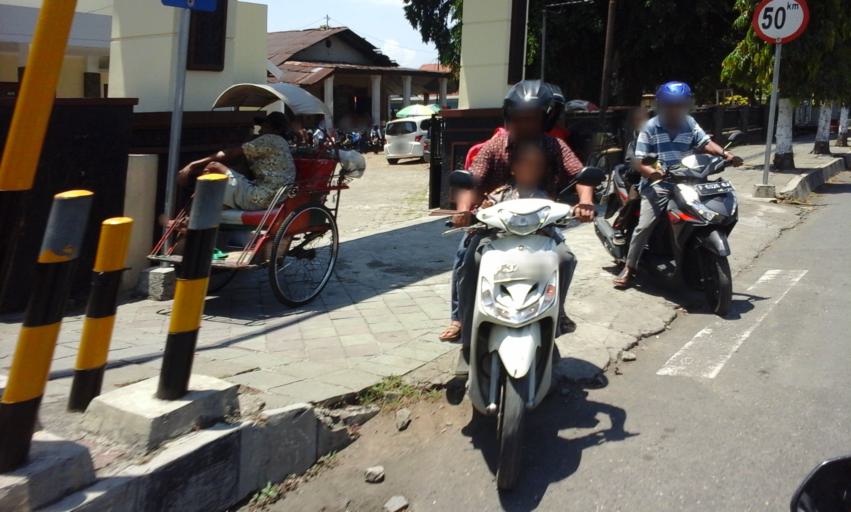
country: ID
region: East Java
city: Krajan
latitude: -8.1617
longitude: 113.7080
